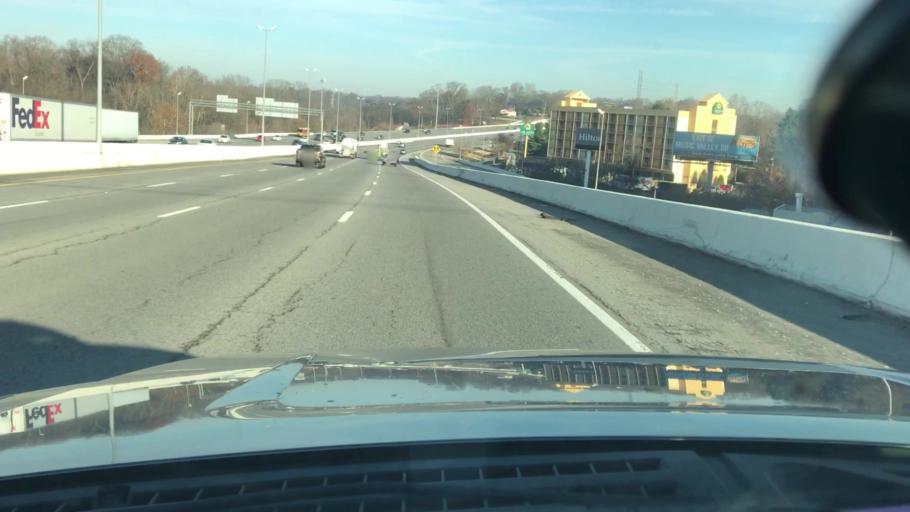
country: US
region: Tennessee
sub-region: Davidson County
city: Nashville
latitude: 36.1530
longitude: -86.6909
